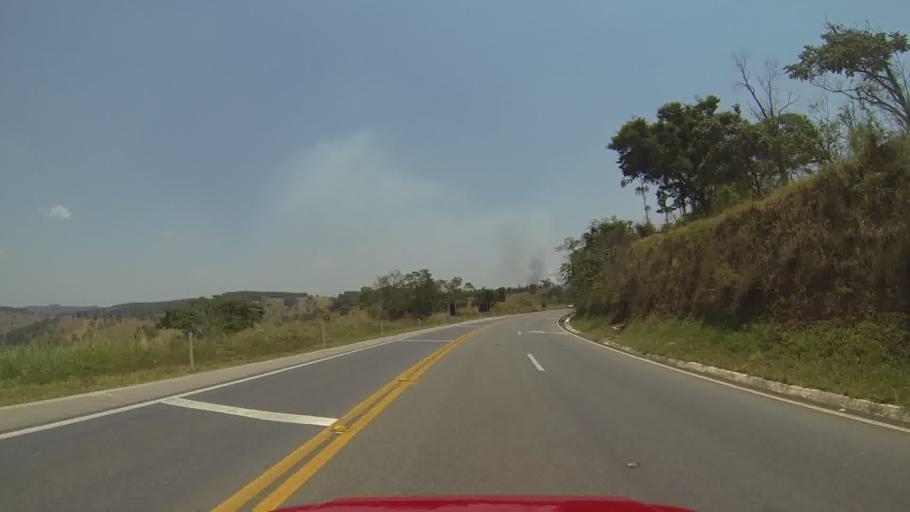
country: BR
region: Minas Gerais
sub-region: Itapecerica
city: Itapecerica
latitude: -20.3445
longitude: -45.2477
